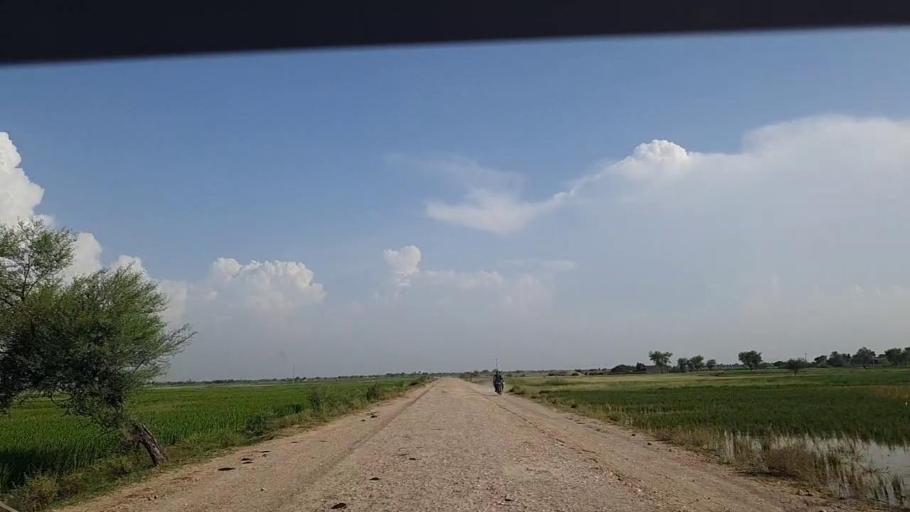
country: PK
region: Sindh
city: Khanpur
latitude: 27.8618
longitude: 69.3752
